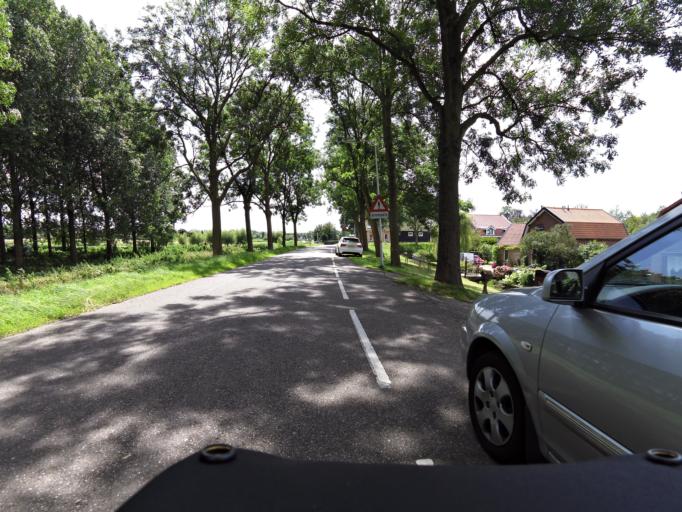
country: NL
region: South Holland
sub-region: Gemeente Albrandswaard
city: Rhoon
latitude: 51.8681
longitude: 4.4107
